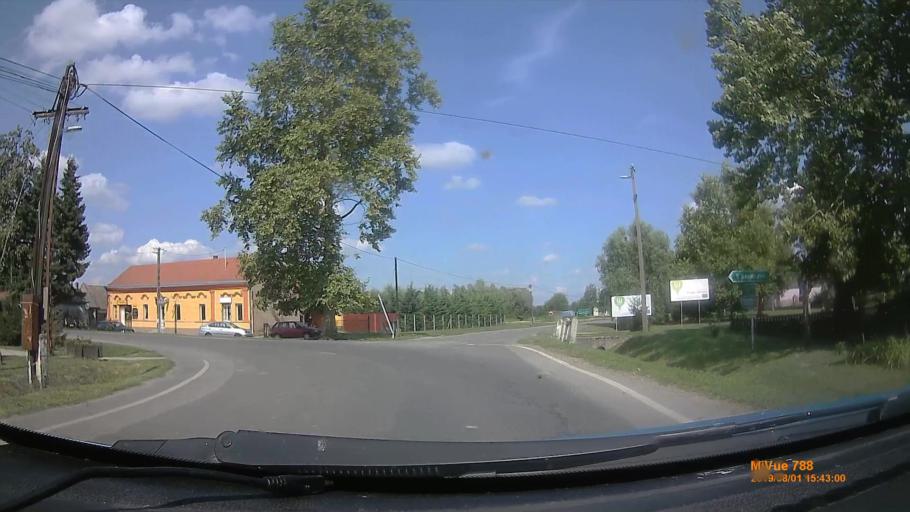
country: HU
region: Baranya
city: Szentlorinc
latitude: 45.9974
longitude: 17.9686
